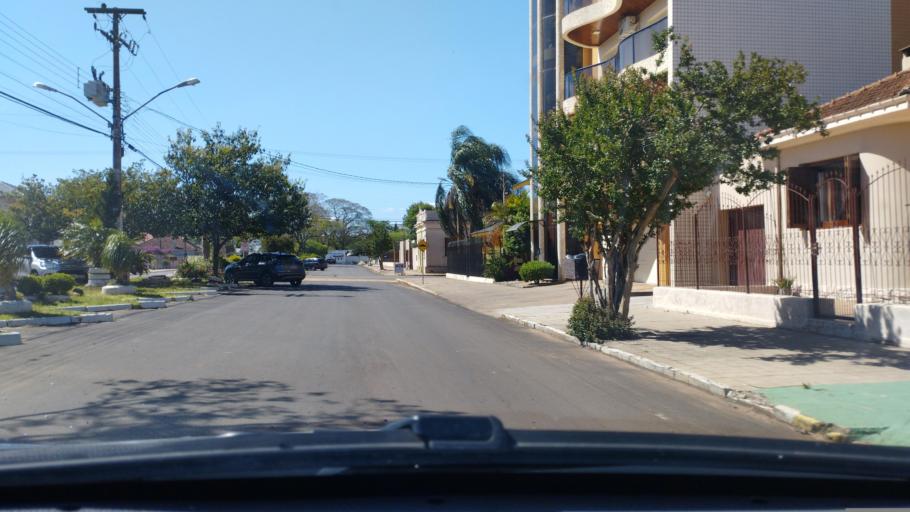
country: BR
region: Rio Grande do Sul
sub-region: Tupancireta
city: Tupancireta
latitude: -29.0767
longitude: -53.8386
